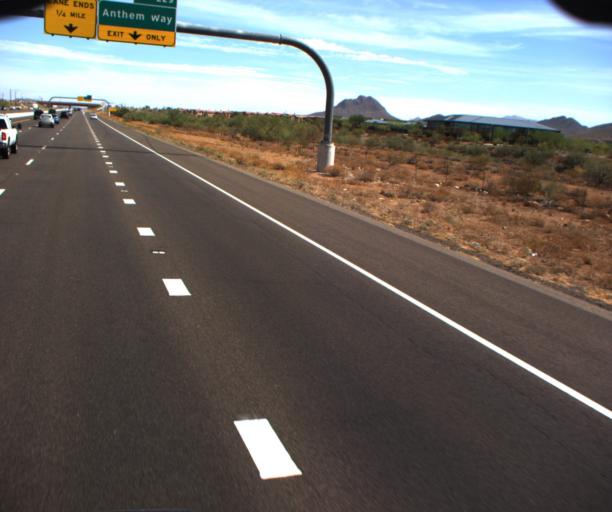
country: US
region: Arizona
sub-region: Maricopa County
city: Anthem
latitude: 33.8607
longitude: -112.1448
